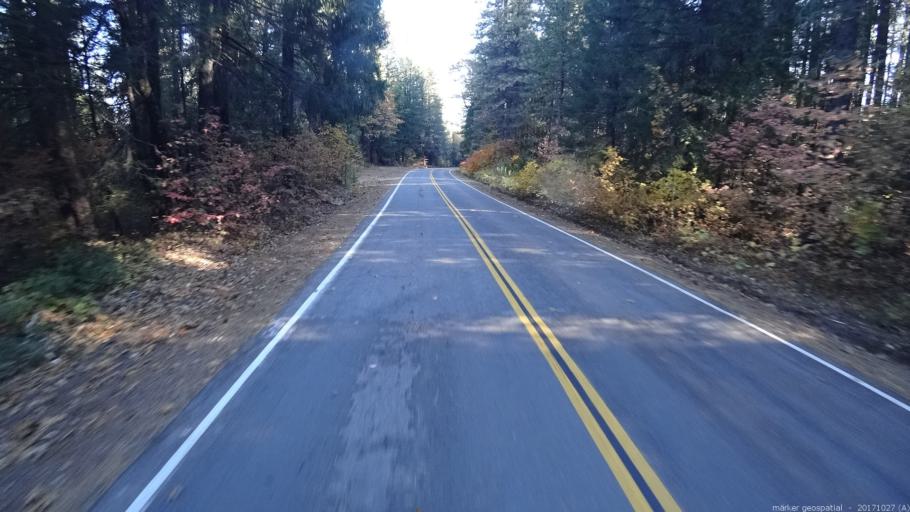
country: US
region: California
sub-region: Shasta County
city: Burney
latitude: 40.9813
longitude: -121.9310
